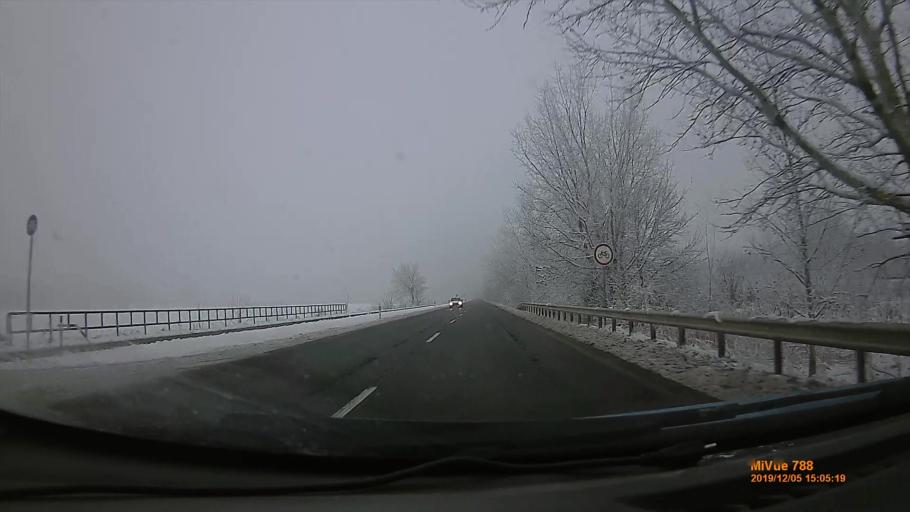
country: HU
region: Szabolcs-Szatmar-Bereg
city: Tiszanagyfalu
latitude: 48.1085
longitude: 21.4883
